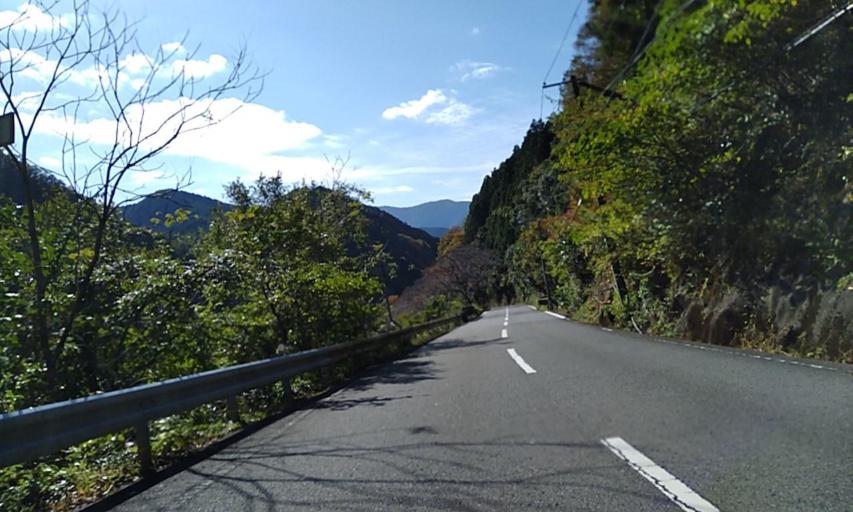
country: JP
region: Wakayama
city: Kainan
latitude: 34.0781
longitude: 135.3584
